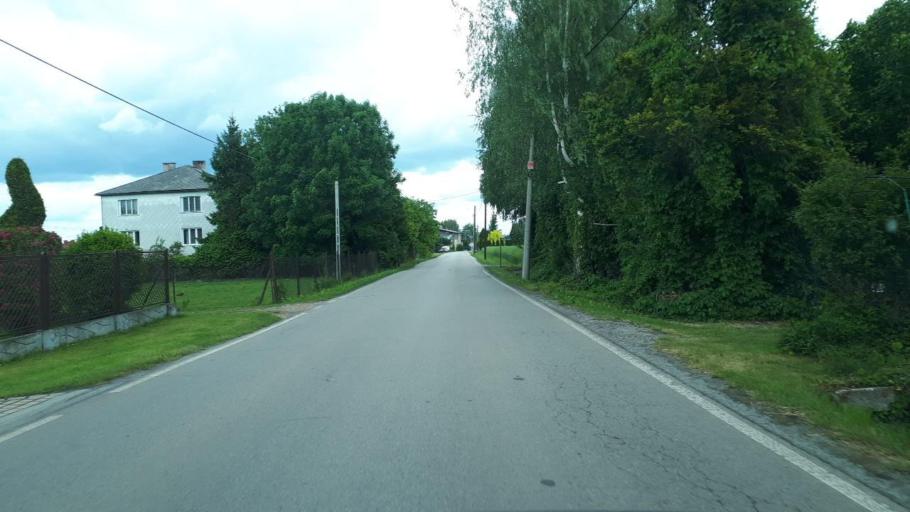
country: PL
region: Silesian Voivodeship
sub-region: Powiat bielski
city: Wilamowice
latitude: 49.9454
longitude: 19.1478
